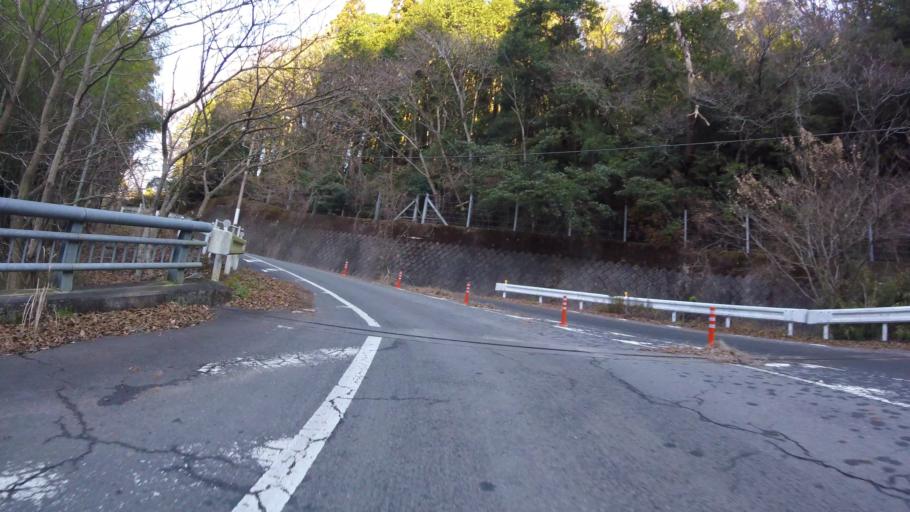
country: JP
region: Kanagawa
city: Yugawara
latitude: 35.1236
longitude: 139.0211
